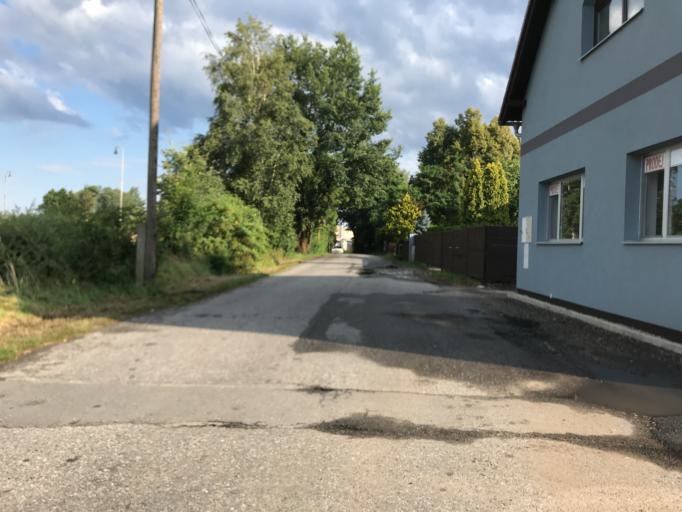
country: CZ
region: Jihocesky
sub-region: Okres Jindrichuv Hradec
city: Trebon
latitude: 49.0164
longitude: 14.7595
